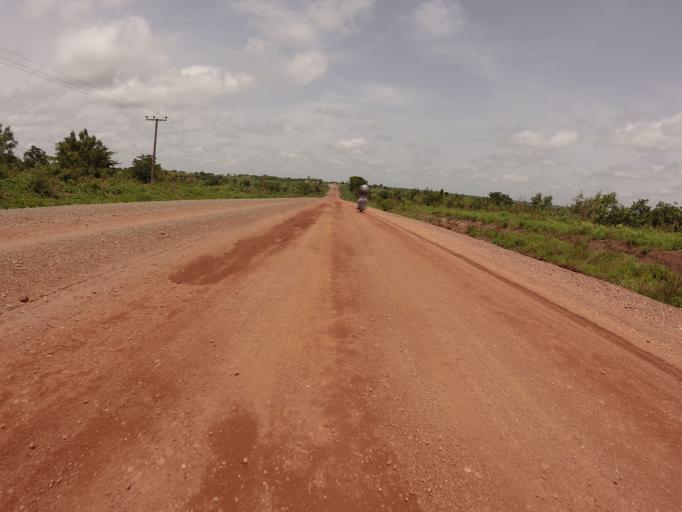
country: GH
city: Kpandae
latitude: 8.6296
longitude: 0.2248
